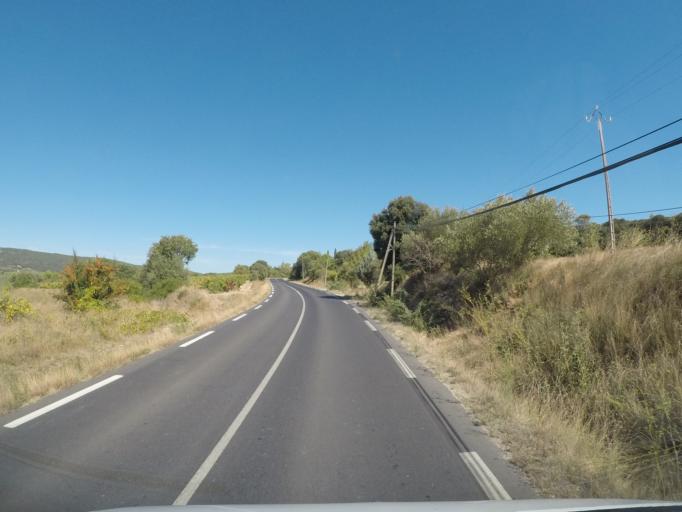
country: FR
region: Languedoc-Roussillon
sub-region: Departement de l'Herault
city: Aniane
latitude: 43.6968
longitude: 3.5903
